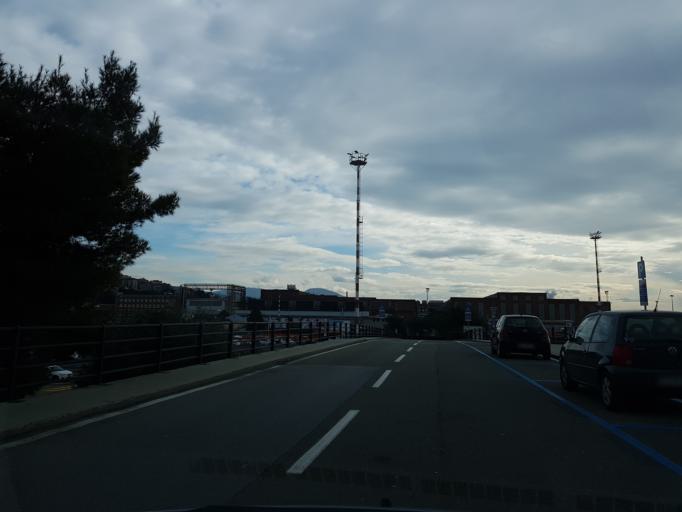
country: IT
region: Liguria
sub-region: Provincia di Genova
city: San Teodoro
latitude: 44.4149
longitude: 8.8511
